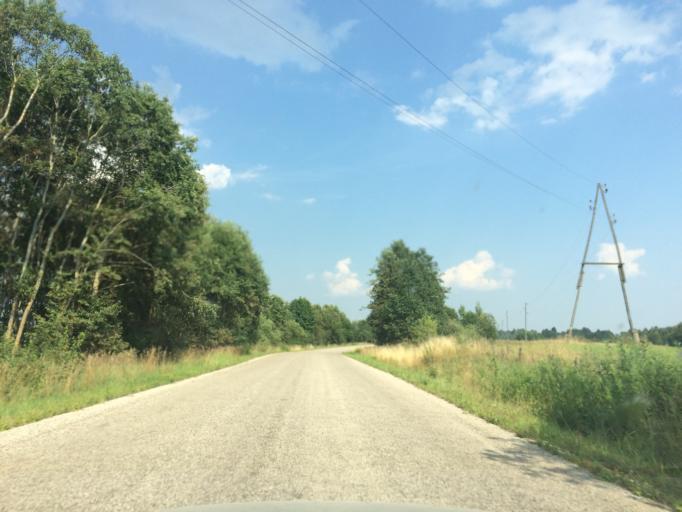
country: LV
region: Rezekne
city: Rezekne
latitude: 56.5558
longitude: 27.4056
